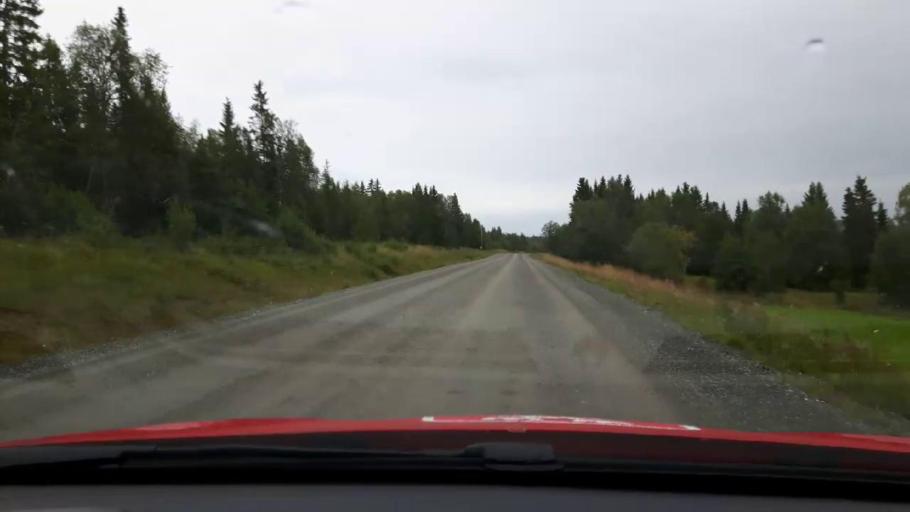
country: SE
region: Jaemtland
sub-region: Are Kommun
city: Are
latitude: 63.4582
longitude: 12.6393
